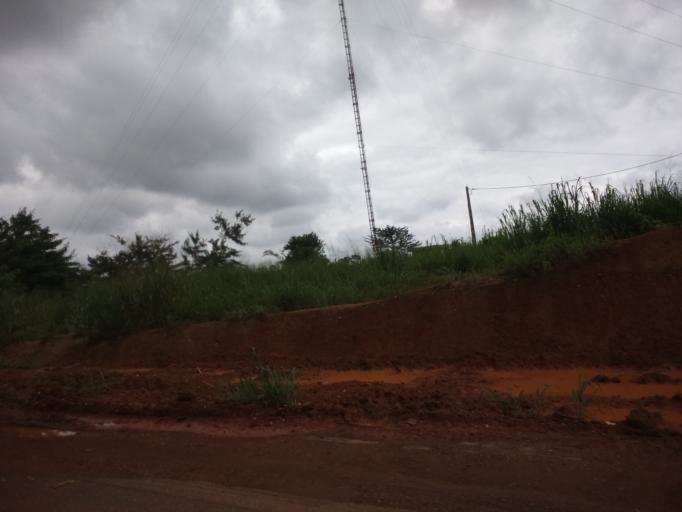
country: CI
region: Moyen-Comoe
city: Abengourou
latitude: 6.6250
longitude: -3.7112
